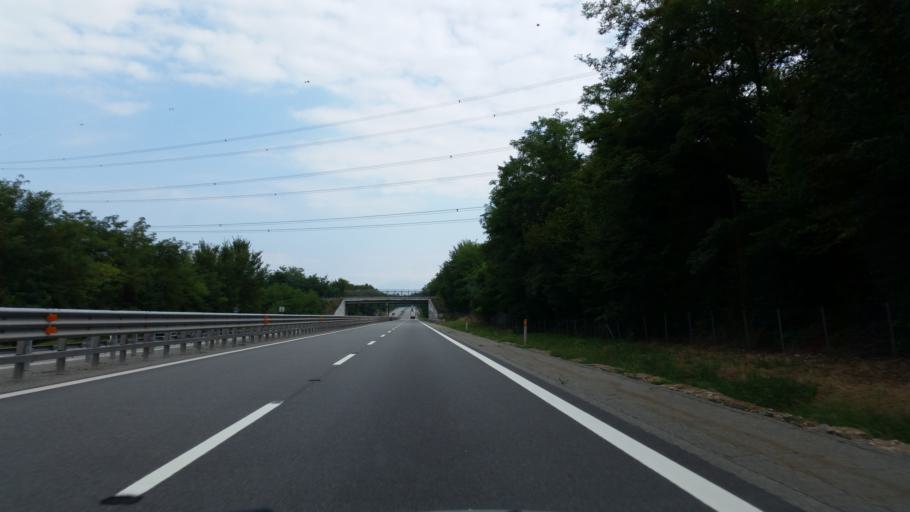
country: IT
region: Piedmont
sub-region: Provincia di Torino
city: Montalenghe
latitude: 45.3319
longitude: 7.8247
